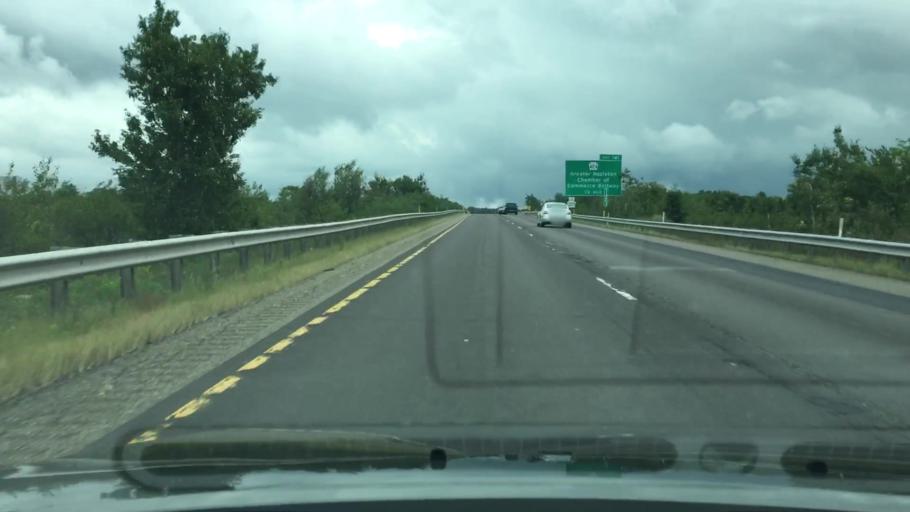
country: US
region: Pennsylvania
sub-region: Luzerne County
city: West Hazleton
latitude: 40.9338
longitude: -76.0186
